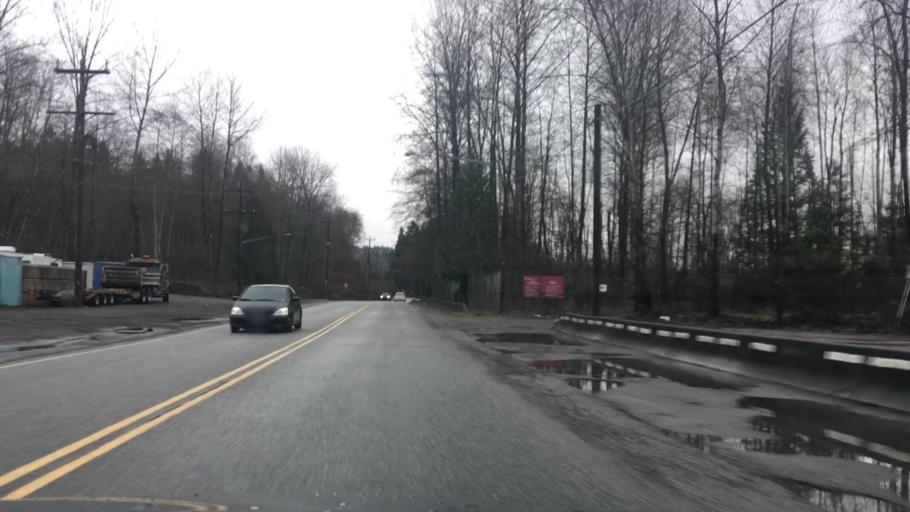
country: CA
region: British Columbia
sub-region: Fraser Valley Regional District
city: North Vancouver
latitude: 49.3079
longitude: -123.0042
